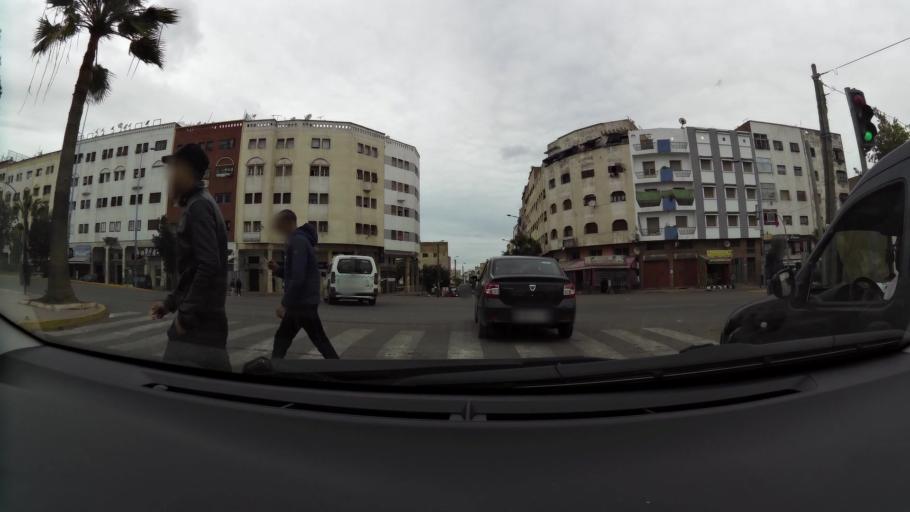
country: MA
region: Grand Casablanca
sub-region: Mediouna
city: Tit Mellil
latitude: 33.5679
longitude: -7.5385
